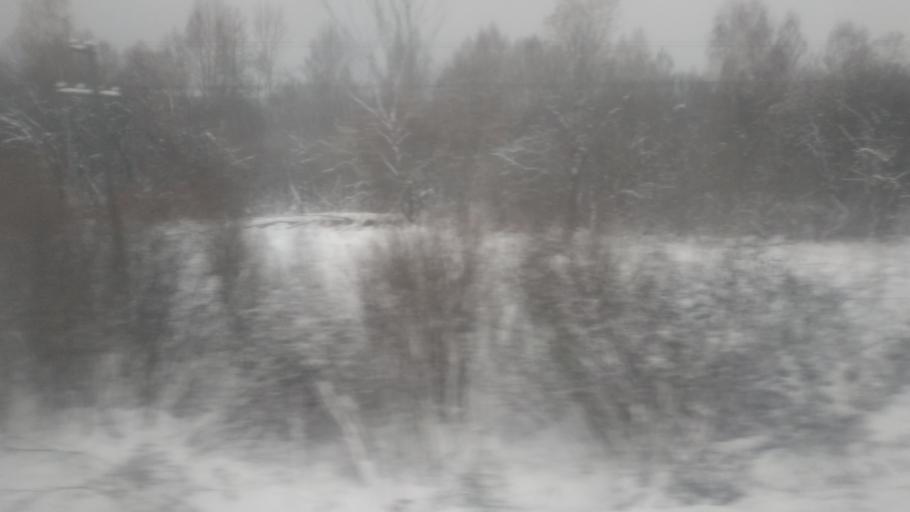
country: RU
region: Bashkortostan
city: Amzya
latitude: 56.2394
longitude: 54.5300
